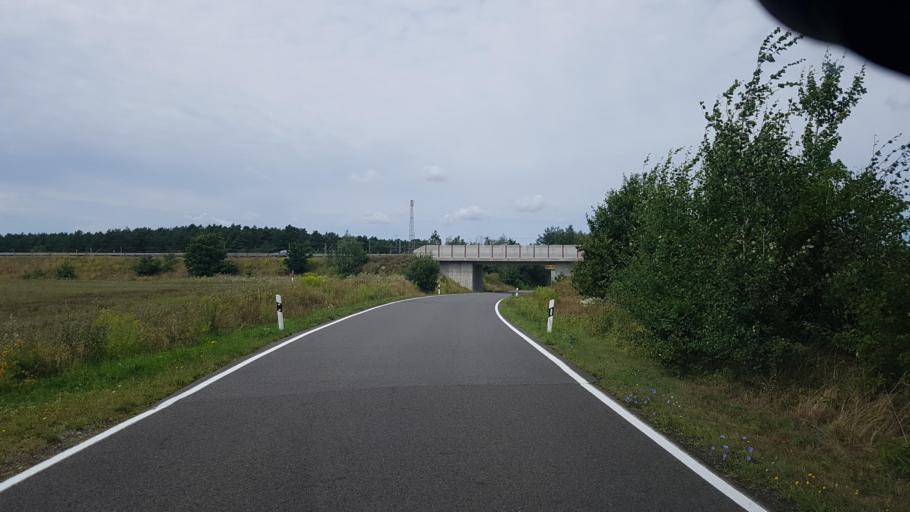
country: DE
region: Brandenburg
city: Spremberg
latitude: 51.5881
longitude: 14.3534
